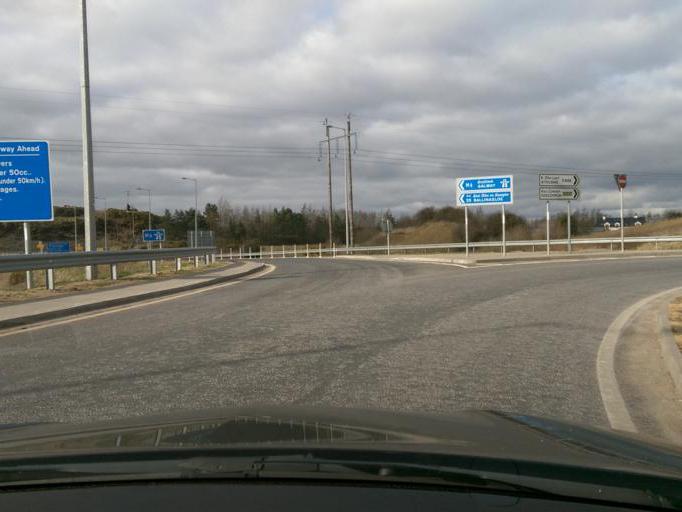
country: IE
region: Leinster
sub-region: An Iarmhi
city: Athlone
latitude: 53.4201
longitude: -7.9773
